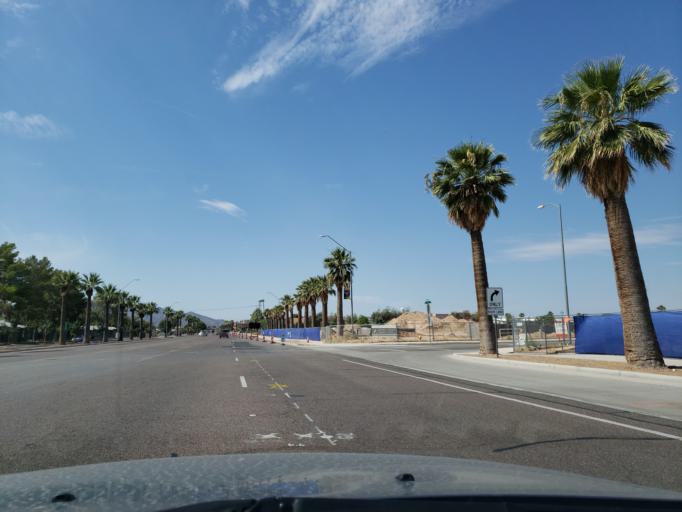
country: US
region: Arizona
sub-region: Maricopa County
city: Goodyear
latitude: 33.4409
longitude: -112.3584
